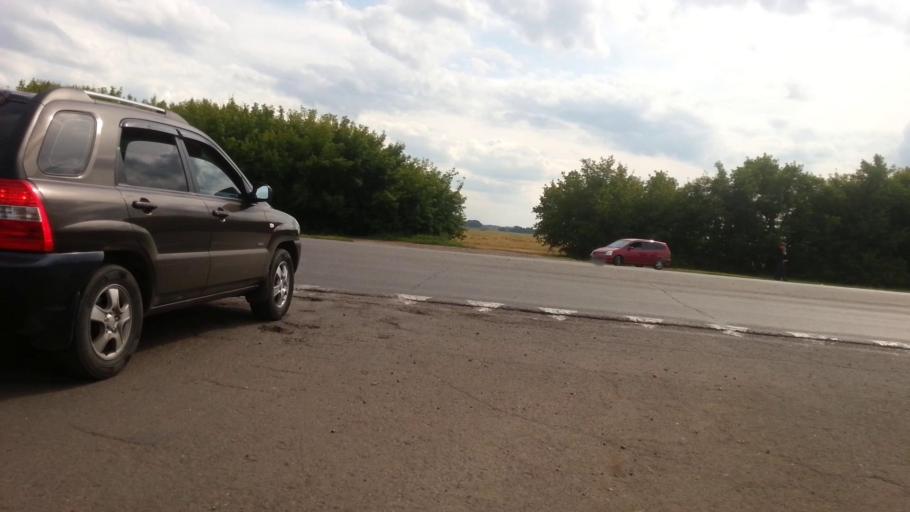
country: RU
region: Altai Krai
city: Nauchnyy Gorodok
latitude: 53.3568
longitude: 83.5079
